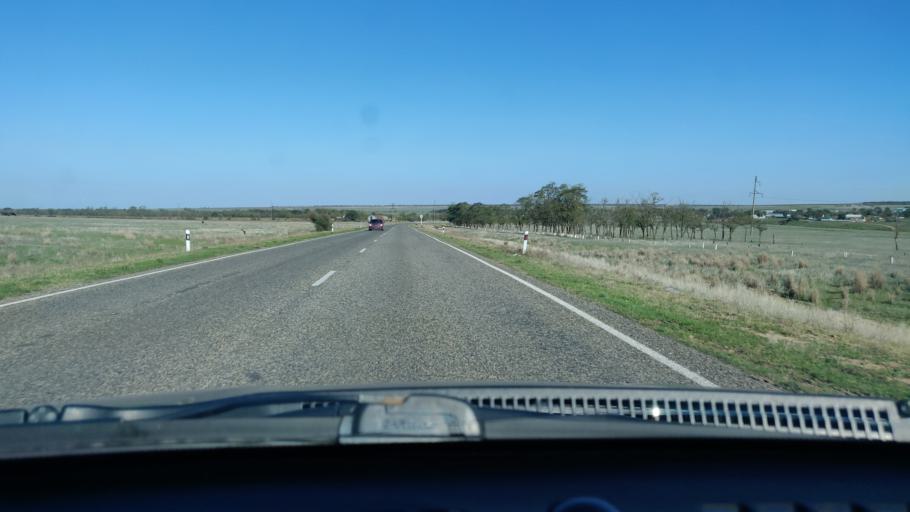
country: RU
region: Stavropol'skiy
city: Letnyaya Stavka
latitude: 45.3765
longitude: 43.6686
